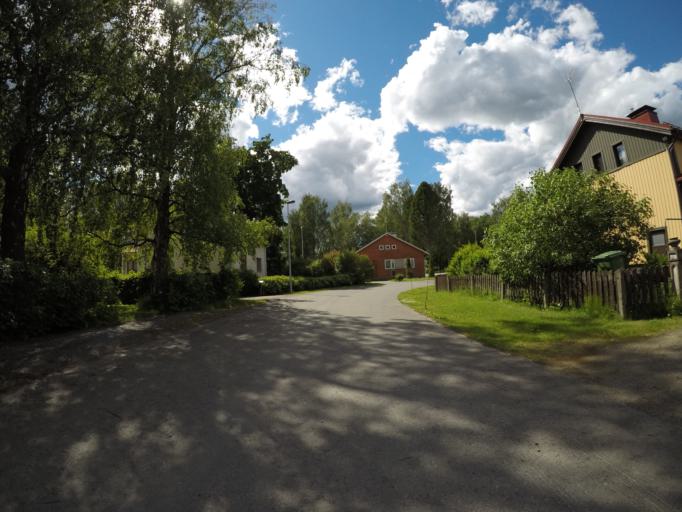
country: FI
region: Haeme
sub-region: Haemeenlinna
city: Haemeenlinna
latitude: 61.0007
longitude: 24.4452
